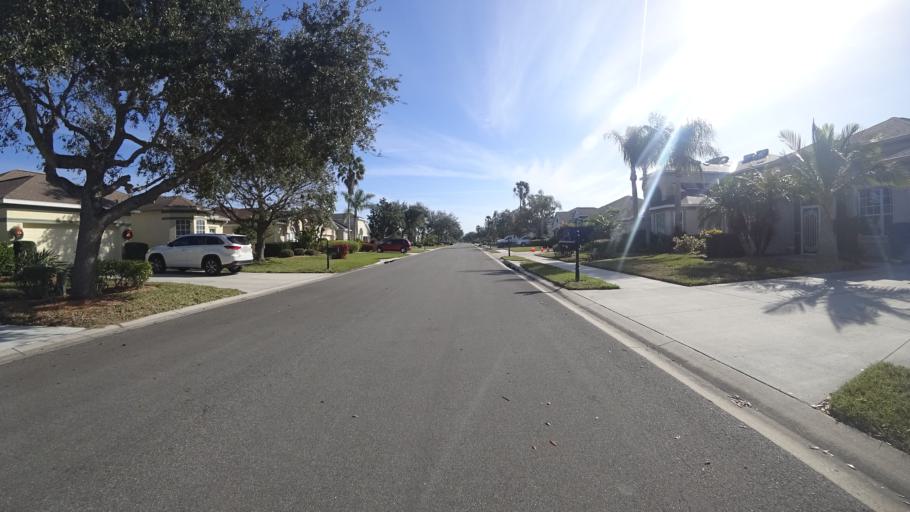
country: US
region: Florida
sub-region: Manatee County
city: Bayshore Gardens
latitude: 27.4485
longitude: -82.6189
